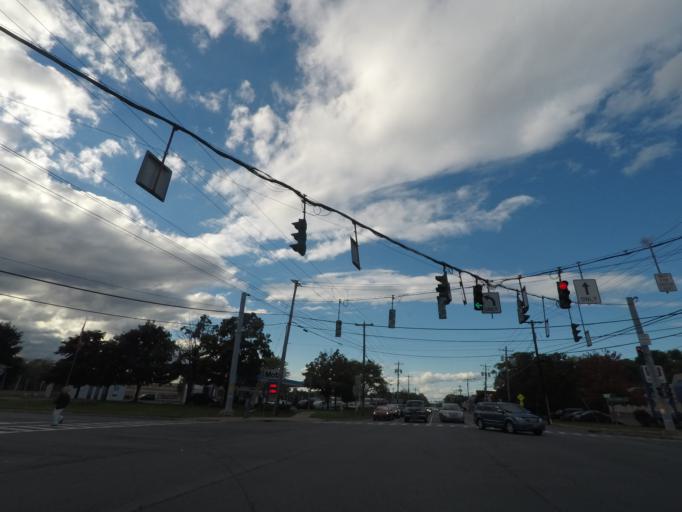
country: US
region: New York
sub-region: Albany County
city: Colonie
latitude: 42.7324
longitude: -73.8498
